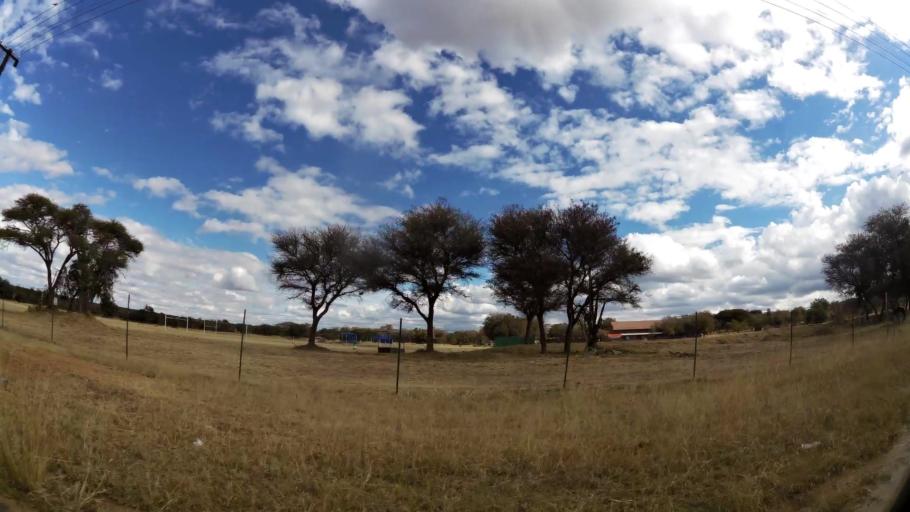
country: ZA
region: Limpopo
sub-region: Waterberg District Municipality
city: Modimolle
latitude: -24.7111
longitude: 28.4024
